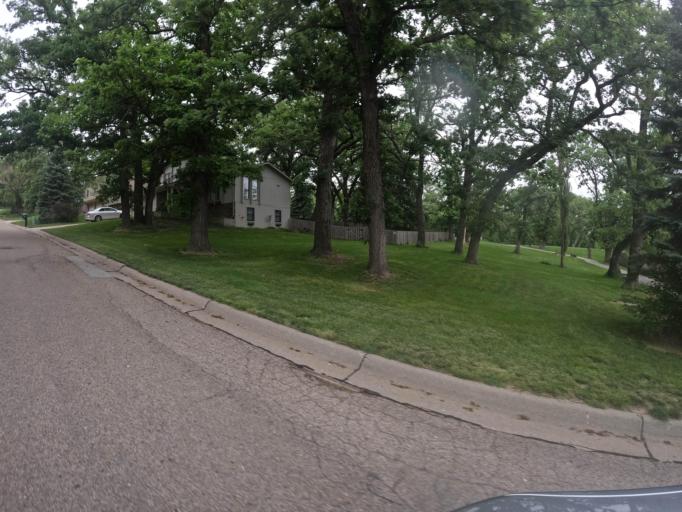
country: US
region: Nebraska
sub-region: Sarpy County
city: Offutt Air Force Base
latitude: 41.0477
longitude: -95.9663
